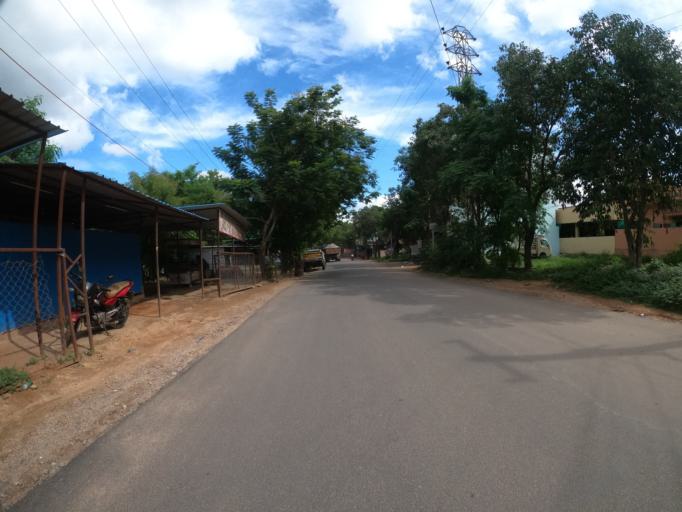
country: IN
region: Telangana
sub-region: Hyderabad
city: Hyderabad
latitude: 17.3564
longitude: 78.3884
